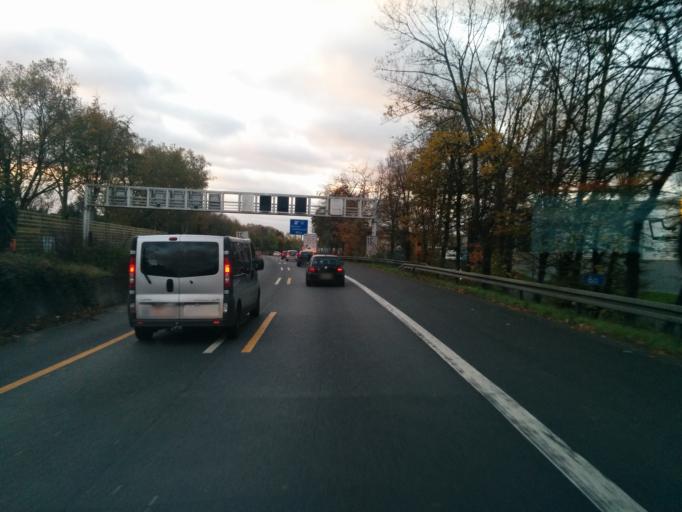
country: DE
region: North Rhine-Westphalia
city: Bochum-Hordel
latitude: 51.4924
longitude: 7.1845
